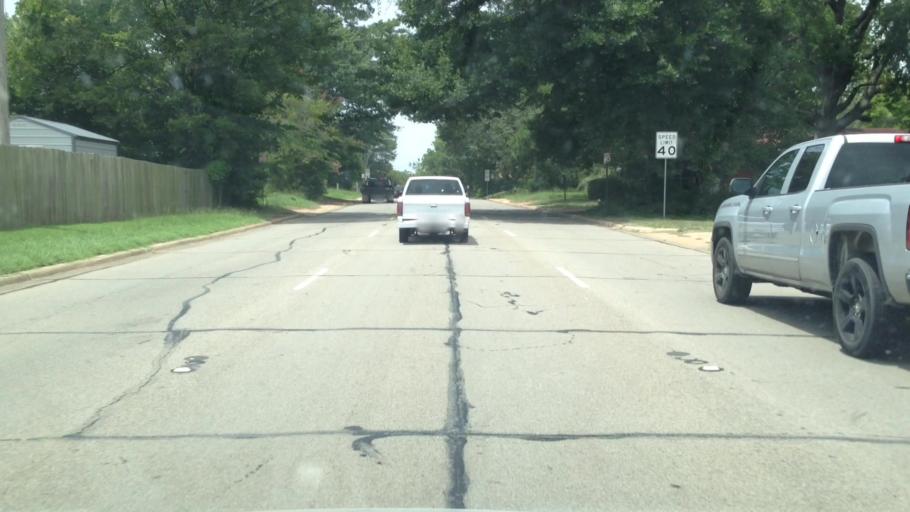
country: US
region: Texas
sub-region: Bowie County
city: Texarkana
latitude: 33.4242
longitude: -94.0570
